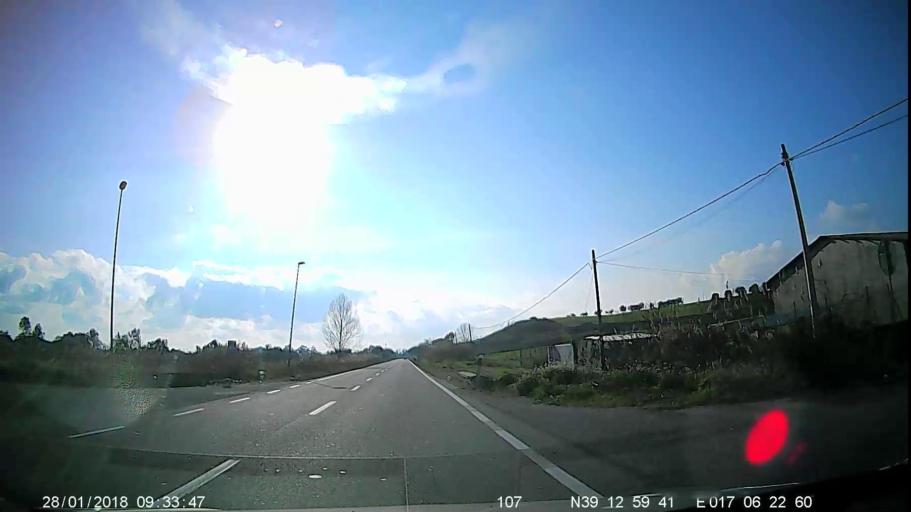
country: IT
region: Calabria
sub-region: Provincia di Crotone
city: Tronca
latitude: 39.2158
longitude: 17.1067
